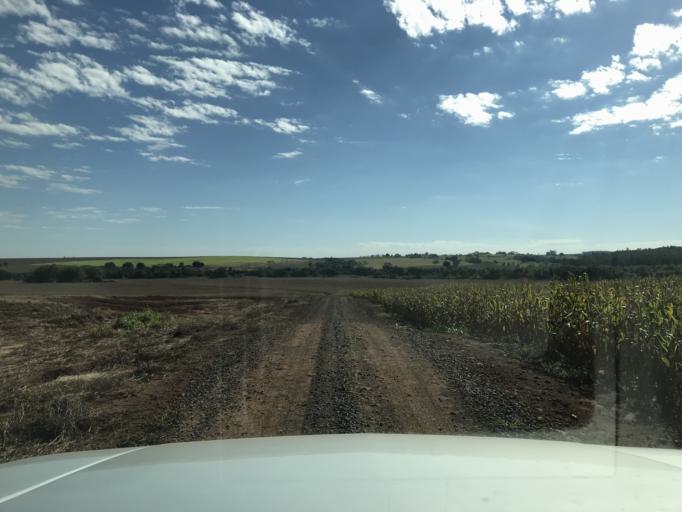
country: BR
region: Parana
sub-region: Palotina
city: Palotina
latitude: -24.1576
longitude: -53.7430
